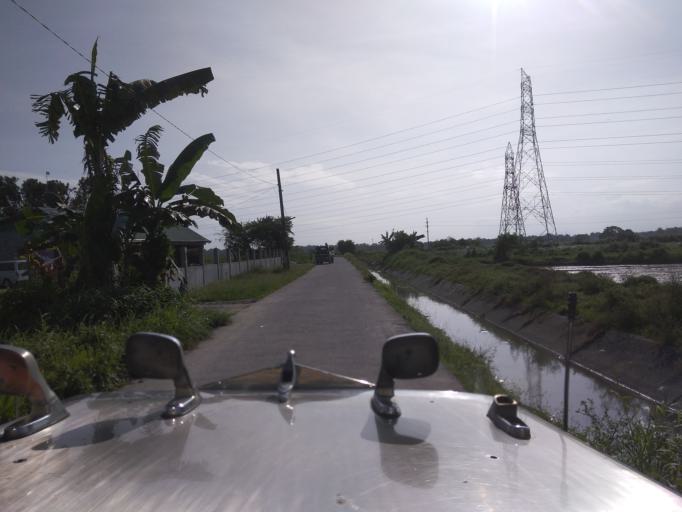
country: PH
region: Central Luzon
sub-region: Province of Pampanga
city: San Patricio
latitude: 15.1035
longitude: 120.7030
